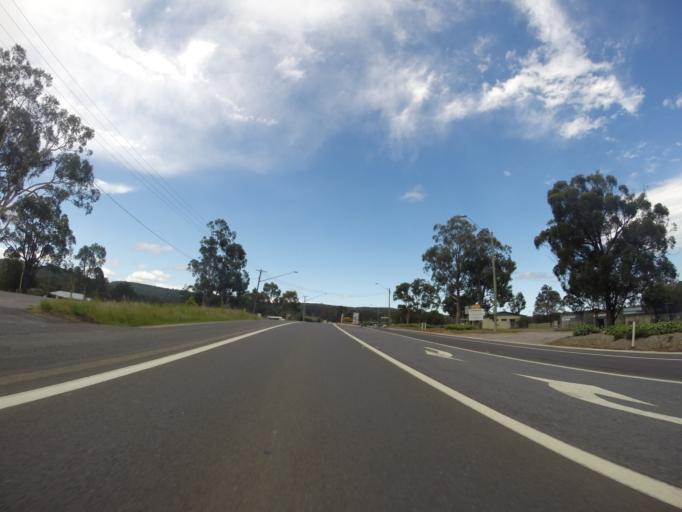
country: AU
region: New South Wales
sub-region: Shoalhaven Shire
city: Falls Creek
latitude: -35.0900
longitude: 150.5092
